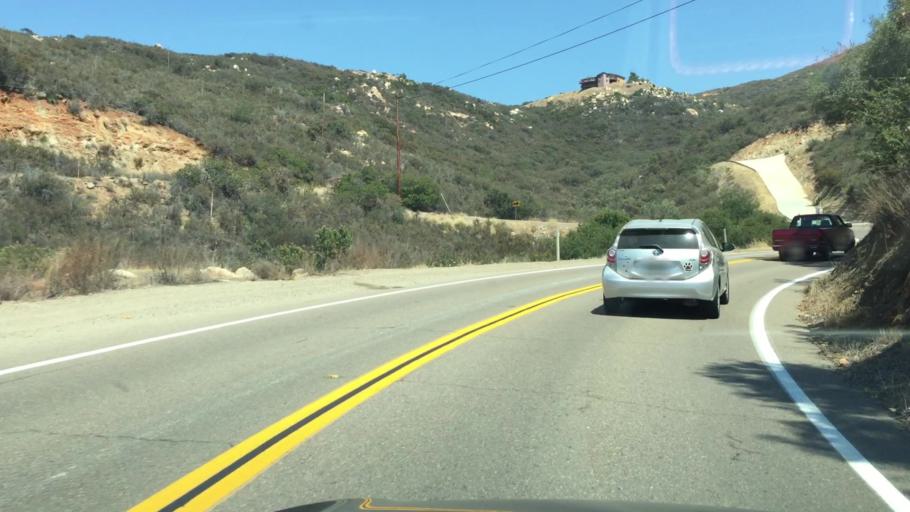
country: US
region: California
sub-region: San Diego County
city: Jamul
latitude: 32.7399
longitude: -116.8122
